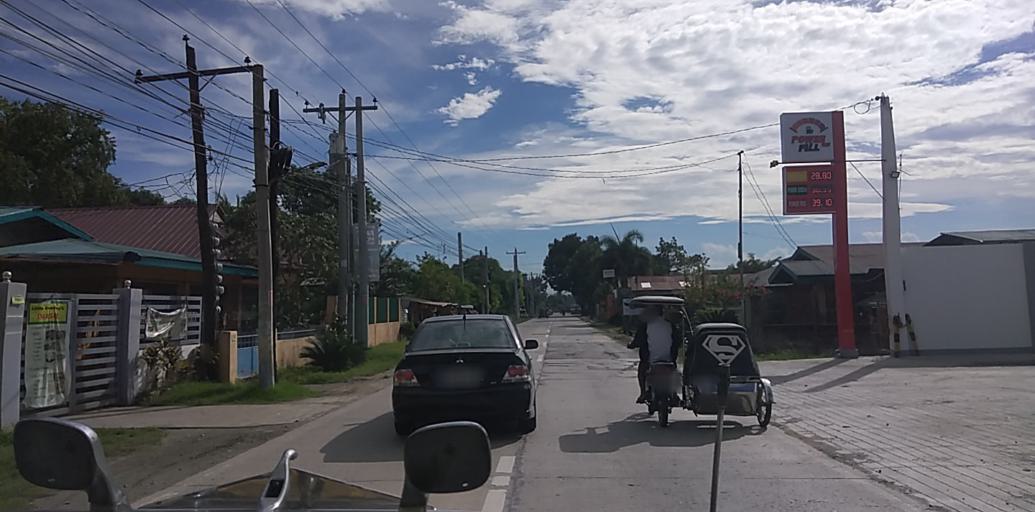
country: PH
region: Central Luzon
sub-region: Province of Pampanga
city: Arayat
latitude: 15.1508
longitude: 120.7457
